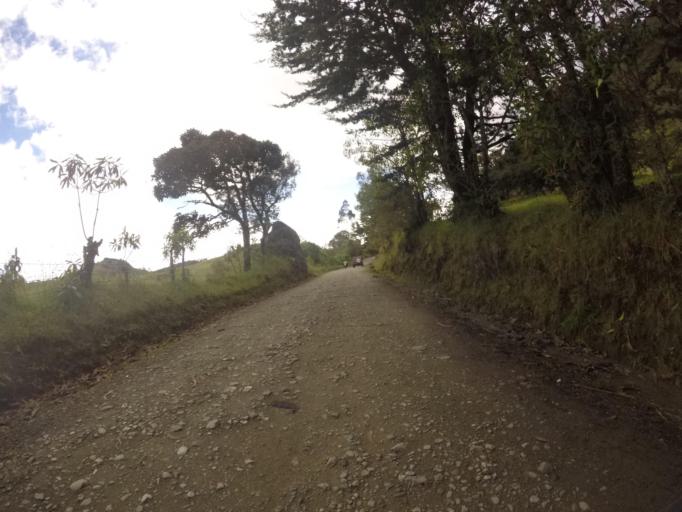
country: CO
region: Cauca
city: Silvia
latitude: 2.6920
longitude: -76.3409
